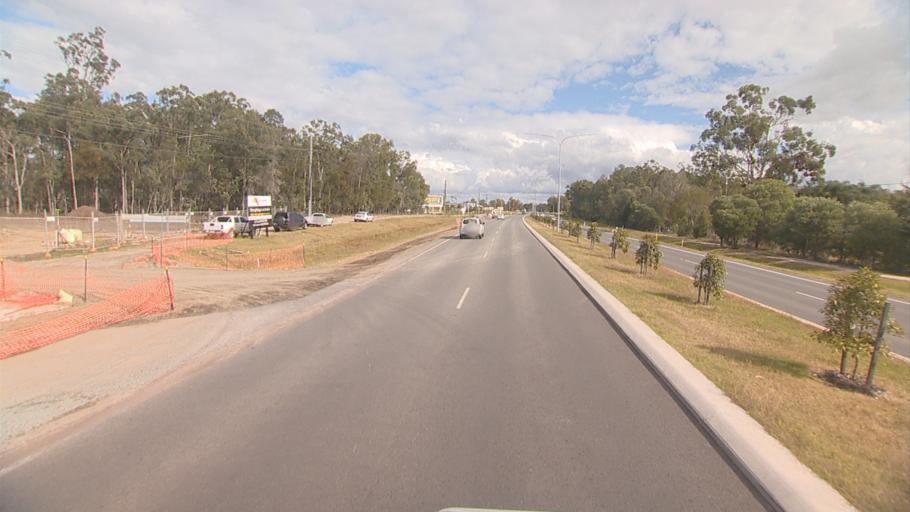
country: AU
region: Queensland
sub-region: Logan
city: Logan Reserve
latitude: -27.7020
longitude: 153.0980
